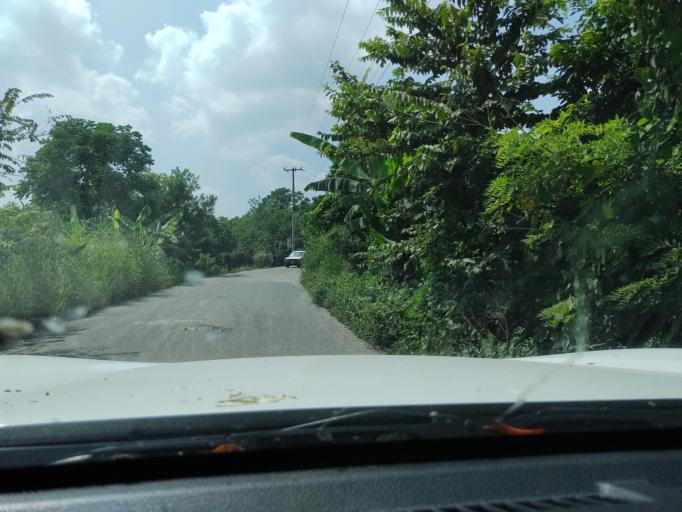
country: MX
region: Veracruz
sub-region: Atzalan
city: Colonias Pedernales
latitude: 20.0604
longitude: -97.0288
